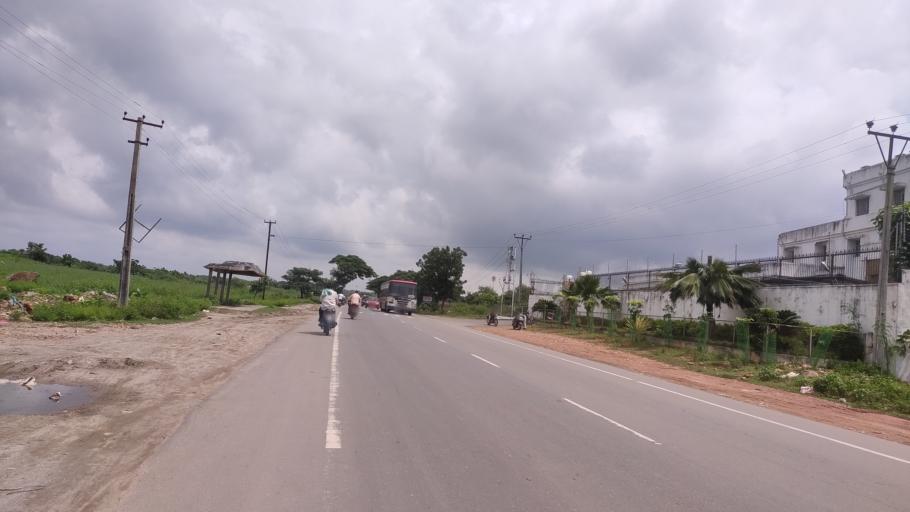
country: IN
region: Telangana
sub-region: Khammam
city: Khammam
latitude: 17.2438
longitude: 80.2022
